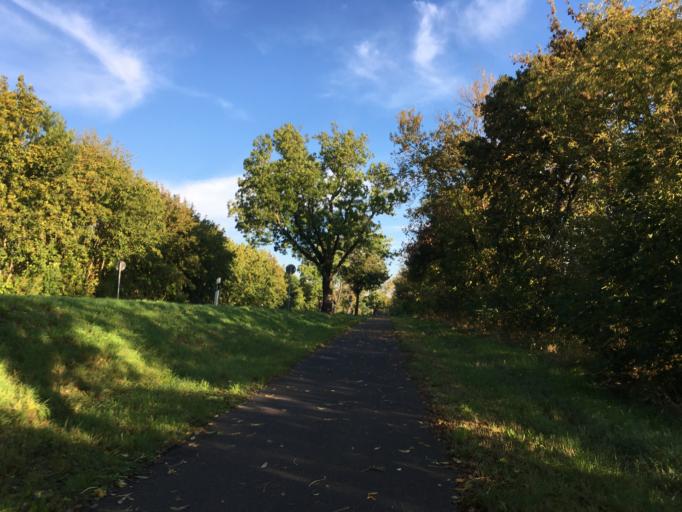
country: DE
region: Brandenburg
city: Frankfurt (Oder)
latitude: 52.3821
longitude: 14.5196
